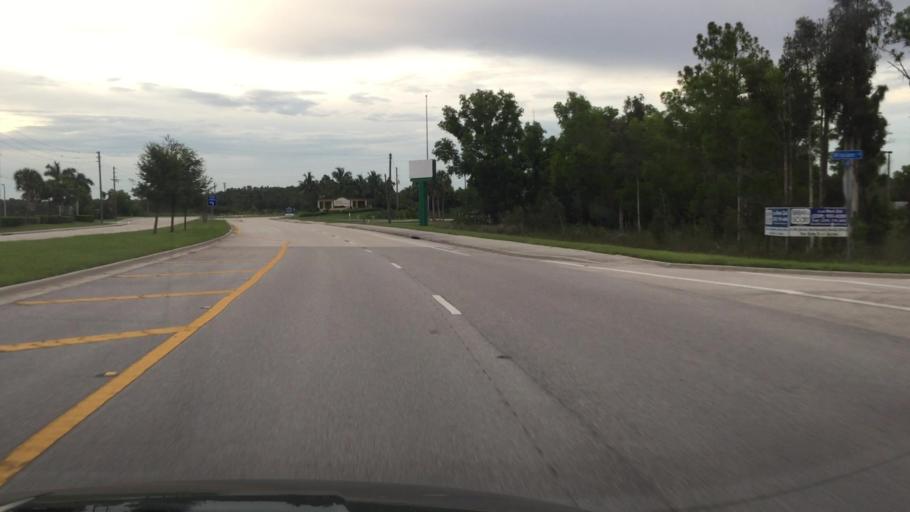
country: US
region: Florida
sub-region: Lee County
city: Gateway
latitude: 26.5492
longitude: -81.7863
